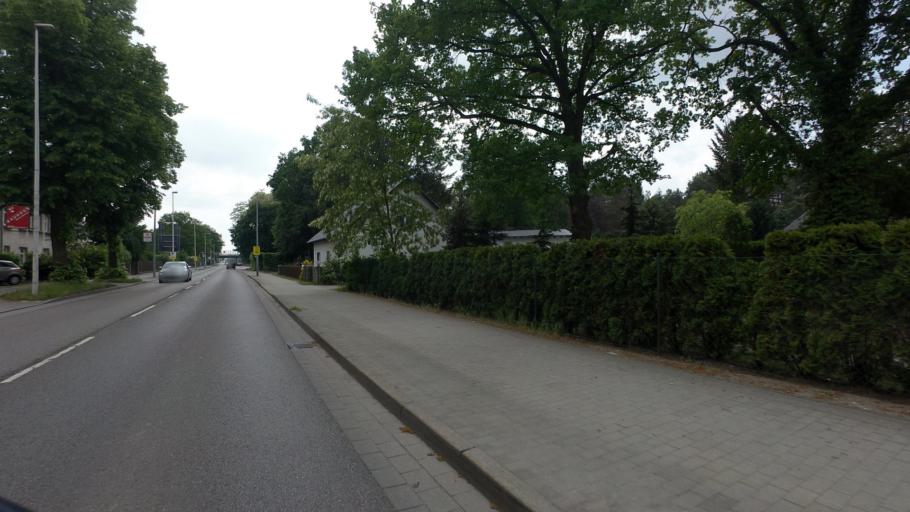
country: DE
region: Brandenburg
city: Cottbus
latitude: 51.7198
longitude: 14.3474
